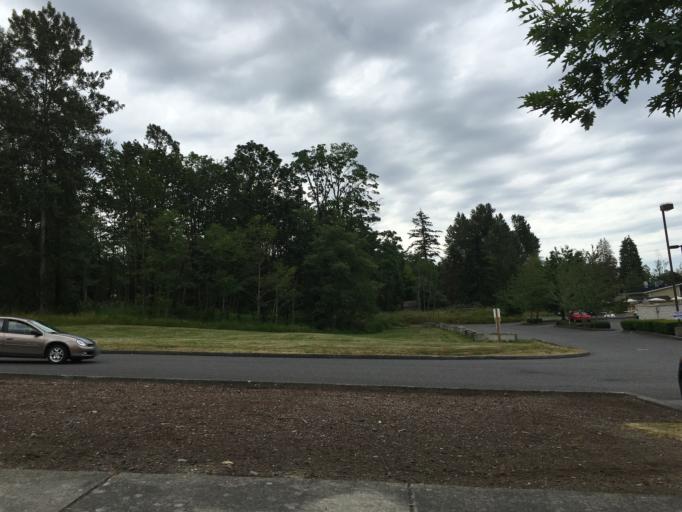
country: US
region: Washington
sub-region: Whatcom County
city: Bellingham
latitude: 48.8006
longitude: -122.4848
